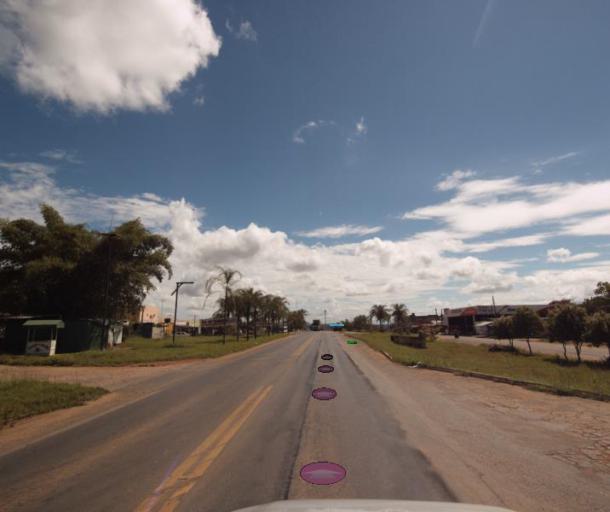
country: BR
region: Goias
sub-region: Uruacu
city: Uruacu
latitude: -14.5272
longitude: -49.1596
